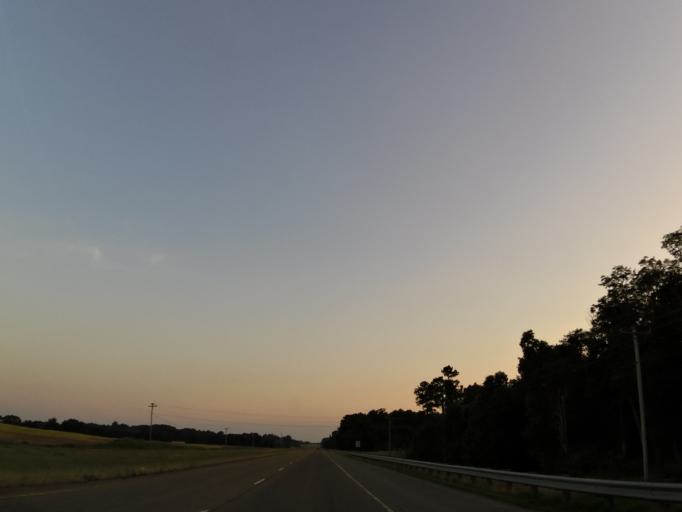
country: US
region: Tennessee
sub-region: Carroll County
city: McKenzie
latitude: 36.1835
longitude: -88.4367
